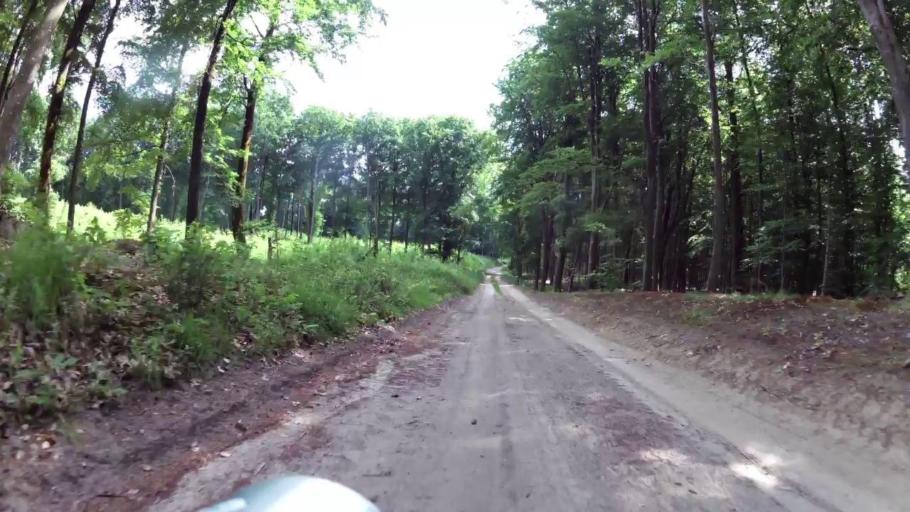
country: PL
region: West Pomeranian Voivodeship
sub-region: Powiat koszalinski
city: Bobolice
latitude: 53.9481
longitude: 16.6788
